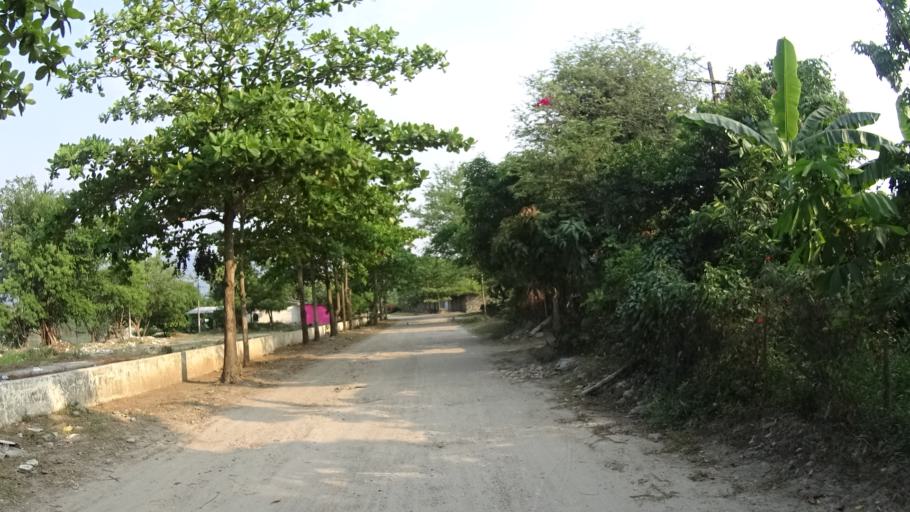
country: CO
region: Caldas
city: La Dorada
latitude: 5.4576
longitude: -74.6631
